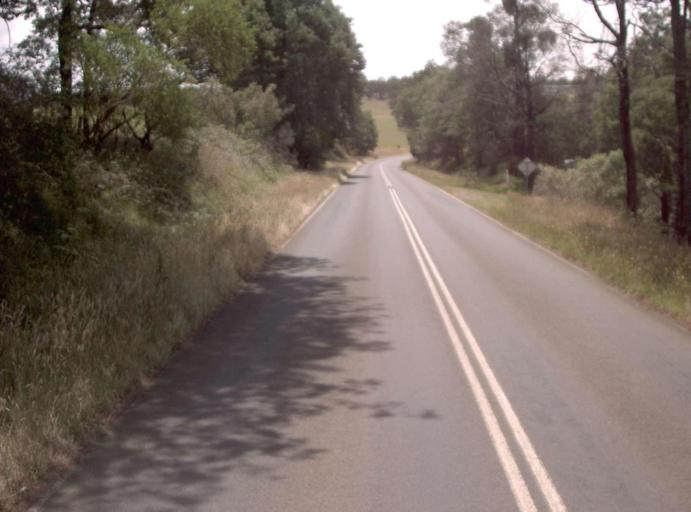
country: AU
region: Victoria
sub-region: Latrobe
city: Moe
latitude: -37.9498
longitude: 146.3900
